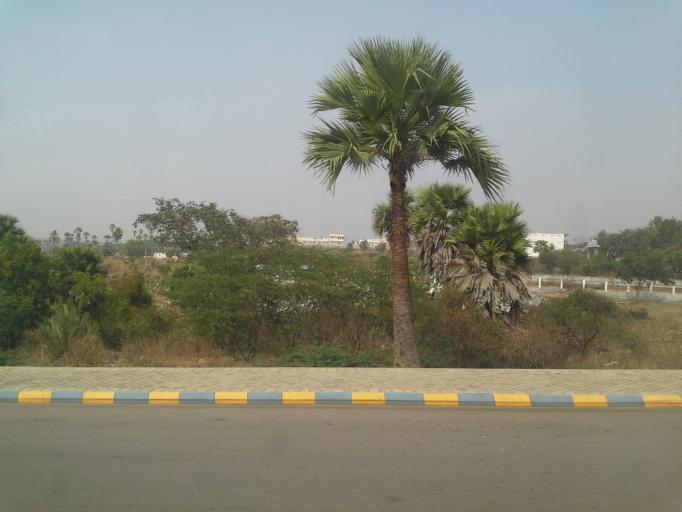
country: IN
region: Telangana
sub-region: Rangareddi
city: Lal Bahadur Nagar
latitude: 17.3112
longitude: 78.6823
